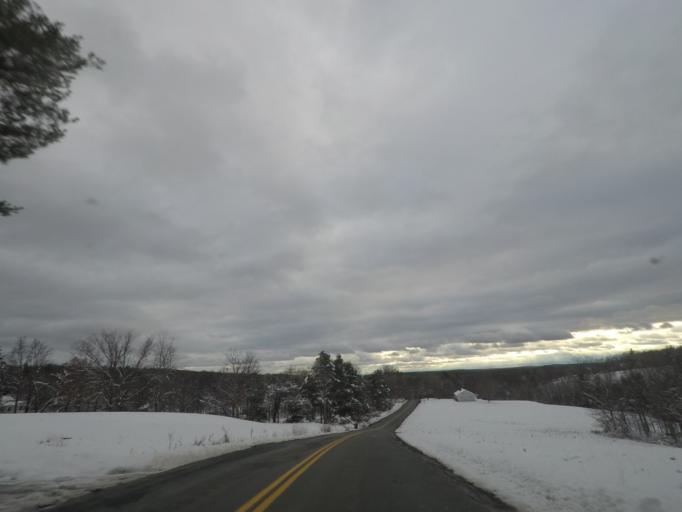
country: US
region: New York
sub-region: Rensselaer County
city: Averill Park
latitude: 42.6603
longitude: -73.5215
